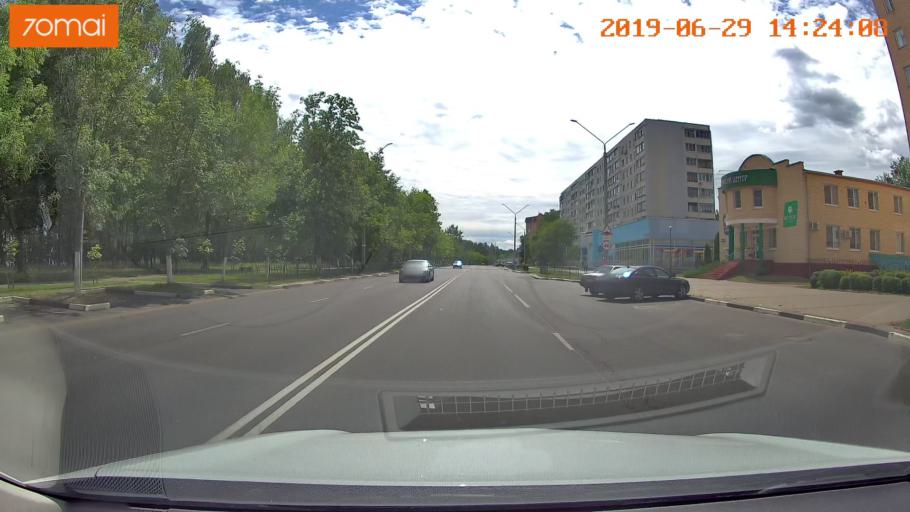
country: BY
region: Minsk
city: Salihorsk
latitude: 52.7820
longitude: 27.5508
